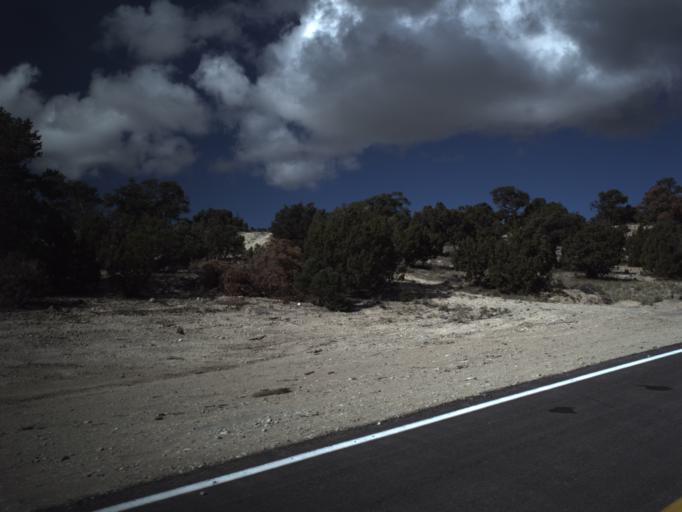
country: US
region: Utah
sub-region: Beaver County
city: Milford
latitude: 38.5136
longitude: -113.5321
